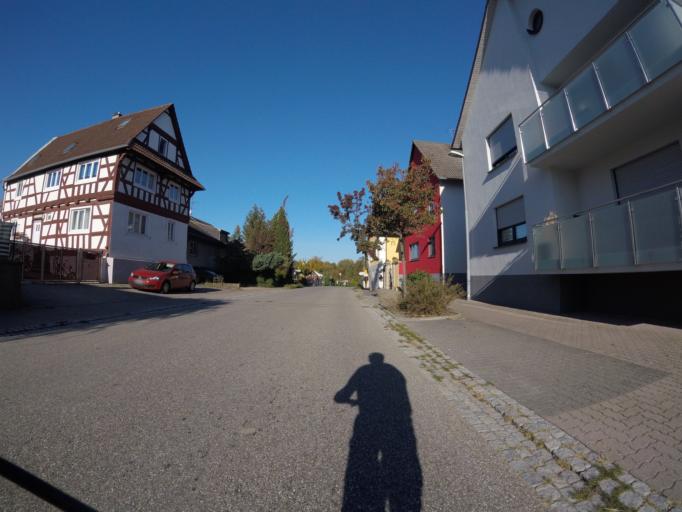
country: DE
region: Baden-Wuerttemberg
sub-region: Karlsruhe Region
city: Eggenstein-Leopoldshafen
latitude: 49.1010
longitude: 8.3889
